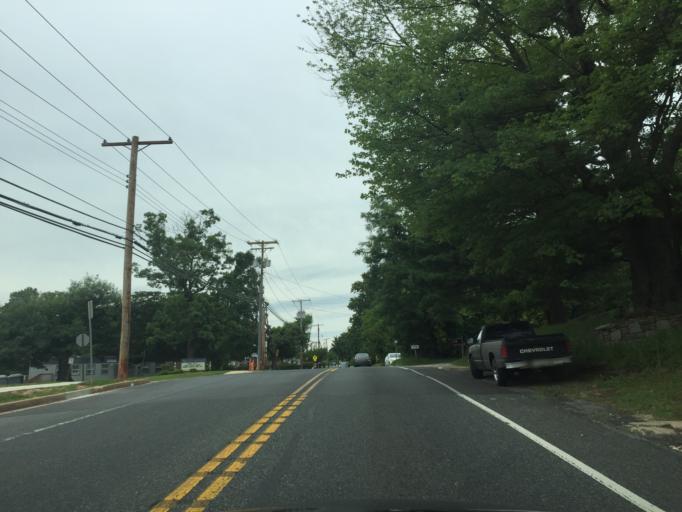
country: US
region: Maryland
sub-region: Baltimore County
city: Overlea
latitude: 39.3490
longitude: -76.5094
